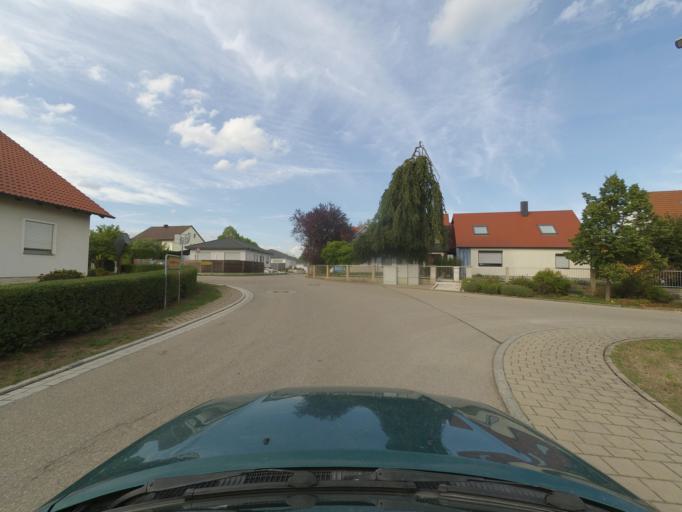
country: DE
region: Bavaria
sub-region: Upper Palatinate
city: Pyrbaum
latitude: 49.2543
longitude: 11.3060
